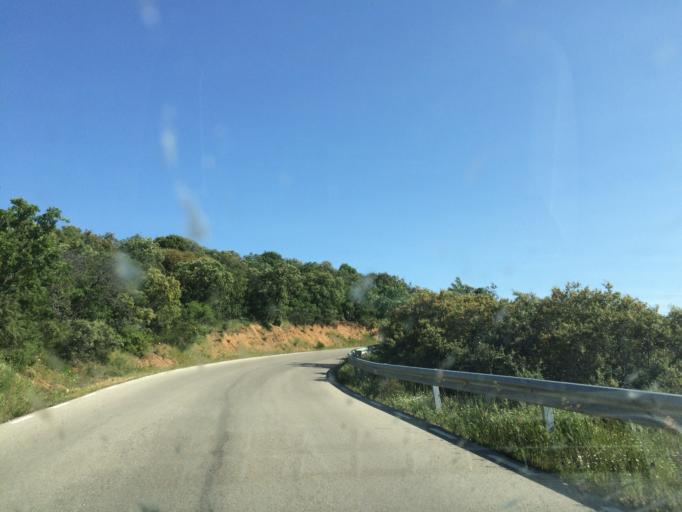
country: ES
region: Madrid
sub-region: Provincia de Madrid
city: Valdepielagos
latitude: 40.7570
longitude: -3.4147
